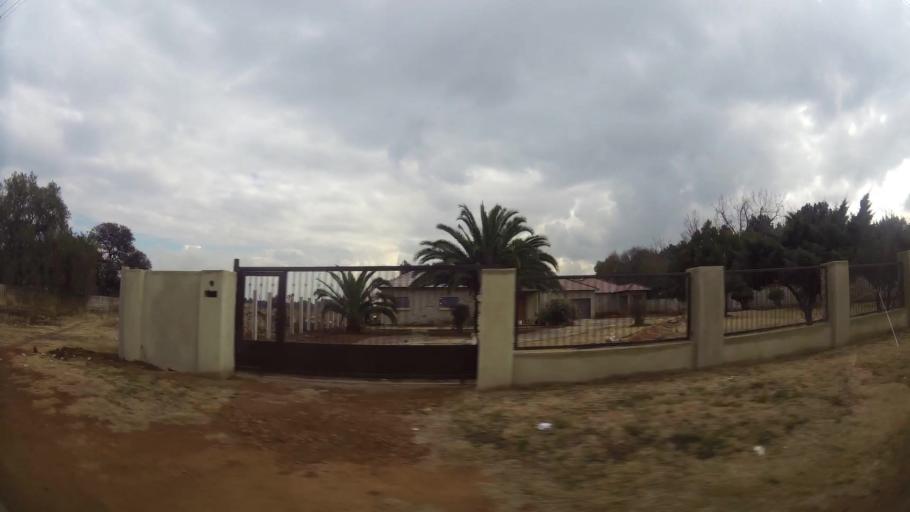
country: ZA
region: Gauteng
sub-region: Sedibeng District Municipality
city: Meyerton
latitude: -26.5858
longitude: 28.0015
